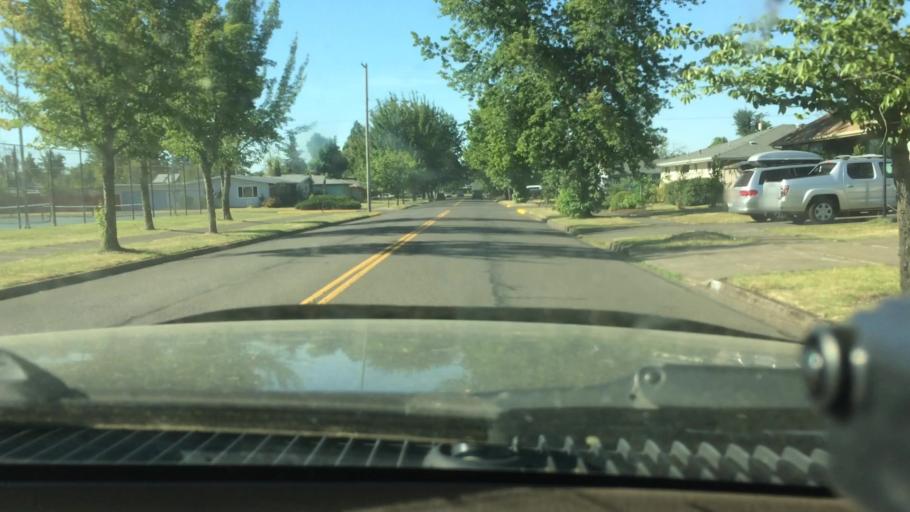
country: US
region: Oregon
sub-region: Lane County
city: Eugene
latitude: 44.0371
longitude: -123.1122
